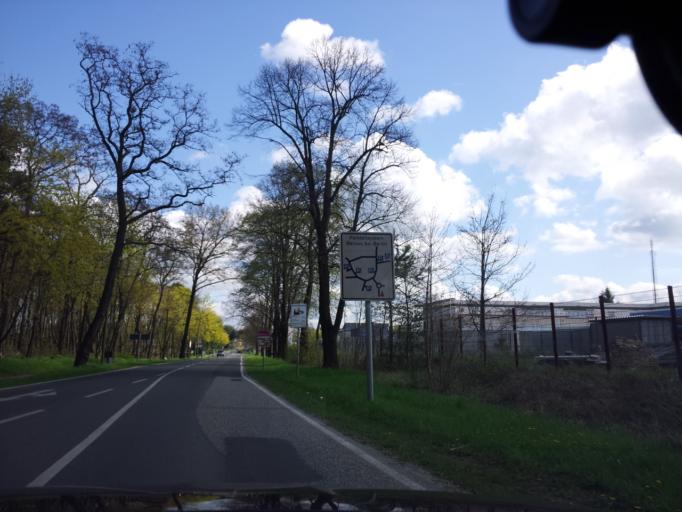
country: DE
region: Brandenburg
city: Bernau bei Berlin
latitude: 52.6877
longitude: 13.5673
